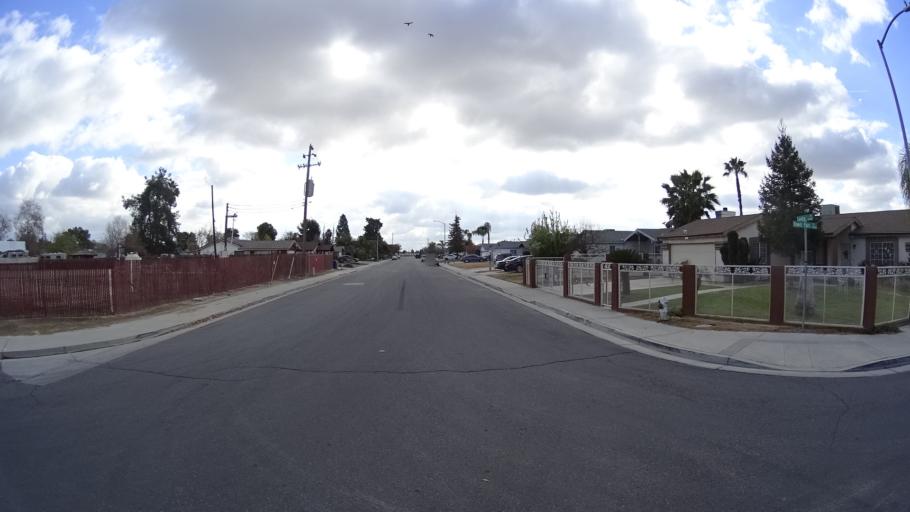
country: US
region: California
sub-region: Kern County
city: Bakersfield
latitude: 35.3578
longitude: -118.9454
